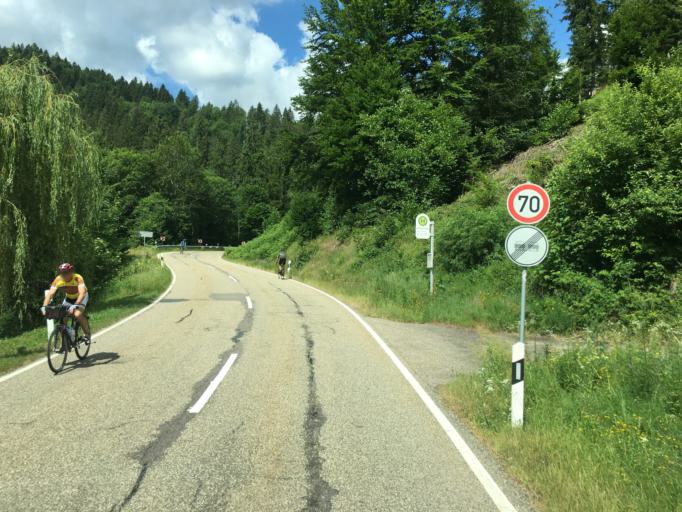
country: DE
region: Baden-Wuerttemberg
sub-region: Karlsruhe Region
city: Forbach
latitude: 48.6369
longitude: 8.3439
